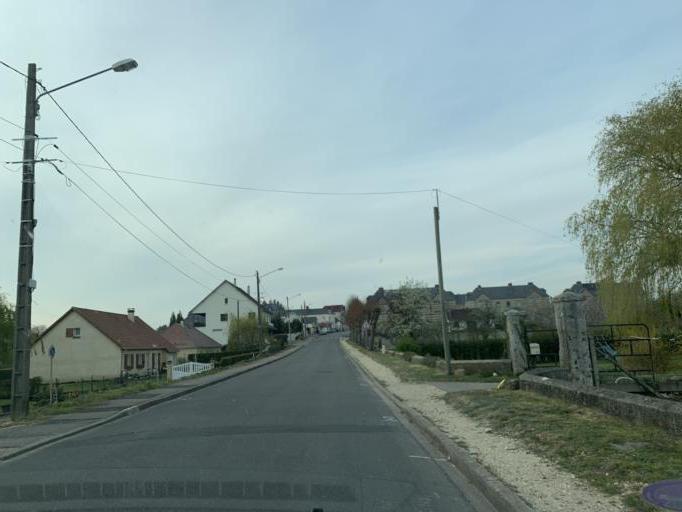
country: FR
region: Haute-Normandie
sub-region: Departement de la Seine-Maritime
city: La Mailleraye-sur-Seine
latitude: 49.4802
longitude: 0.7731
